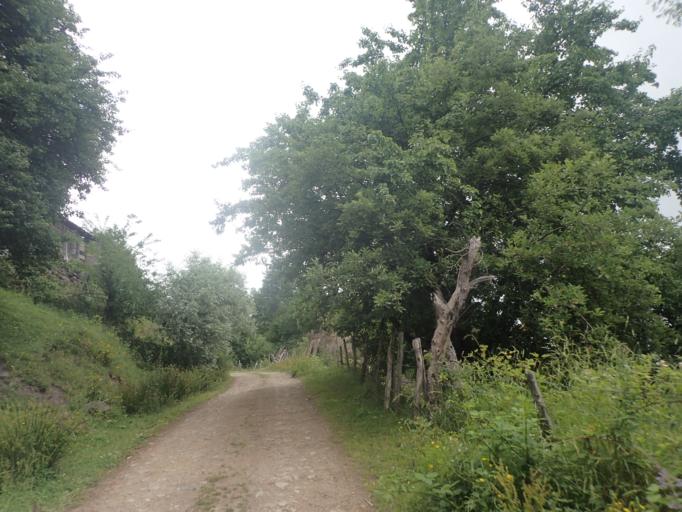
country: TR
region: Ordu
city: Akkus
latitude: 40.8700
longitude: 37.0076
